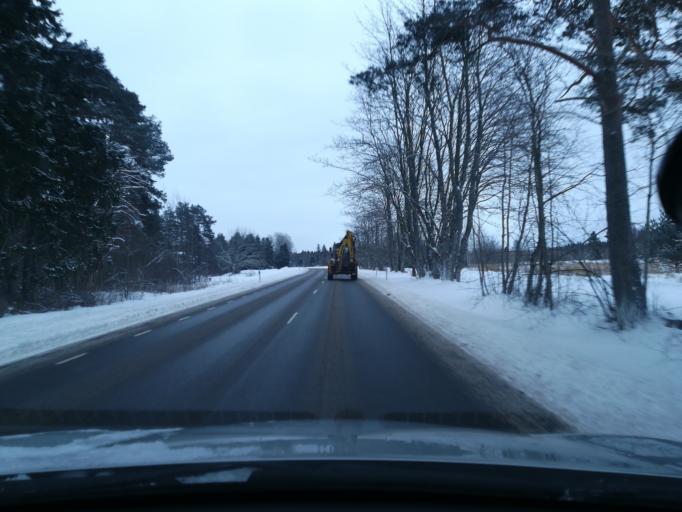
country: EE
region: Harju
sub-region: Keila linn
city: Keila
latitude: 59.3954
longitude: 24.2784
